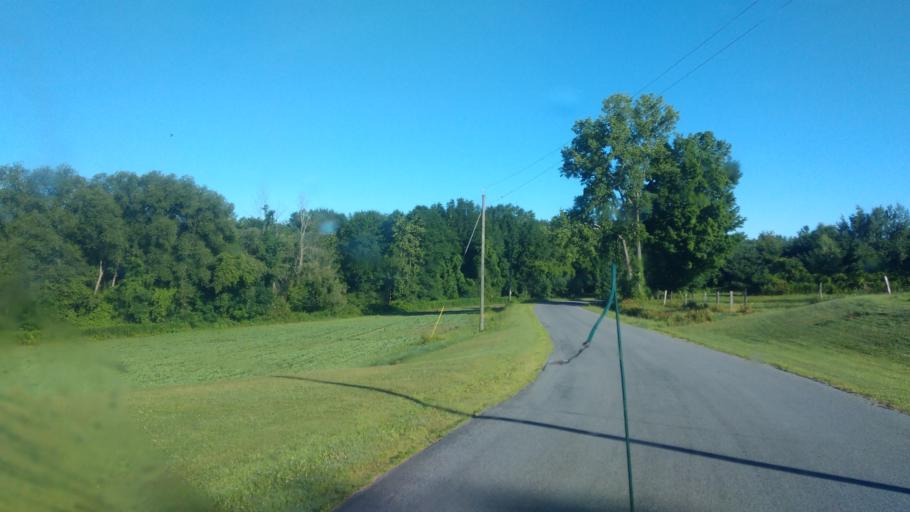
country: US
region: New York
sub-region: Wayne County
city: Lyons
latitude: 43.1382
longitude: -77.0406
